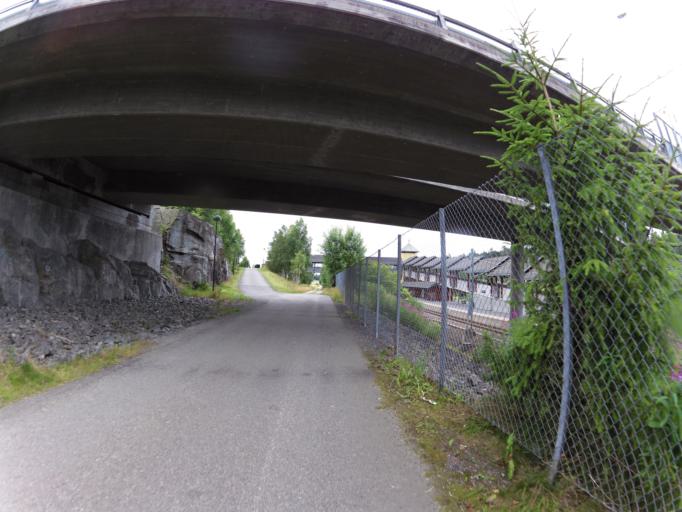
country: NO
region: Akershus
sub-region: Vestby
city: Vestby
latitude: 59.5158
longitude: 10.7264
